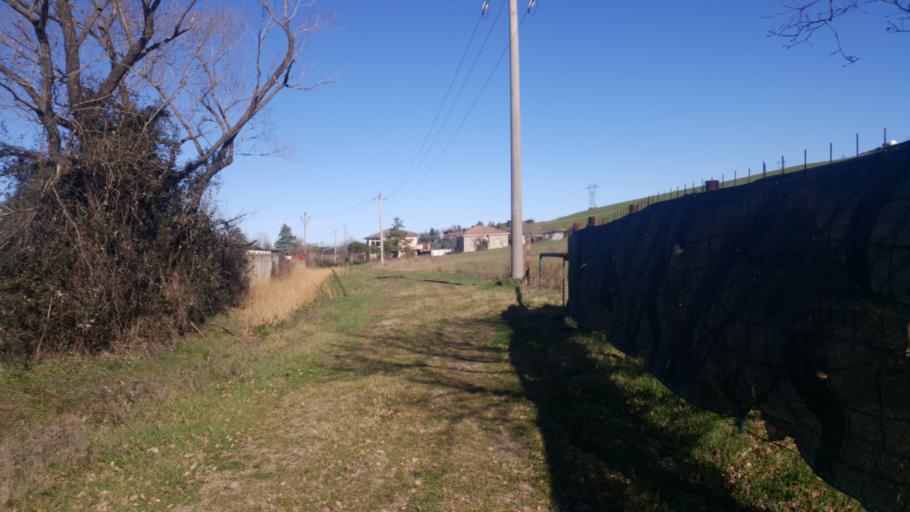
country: IT
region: Emilia-Romagna
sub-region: Provincia di Rimini
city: Cerasolo
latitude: 43.9939
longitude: 12.5394
